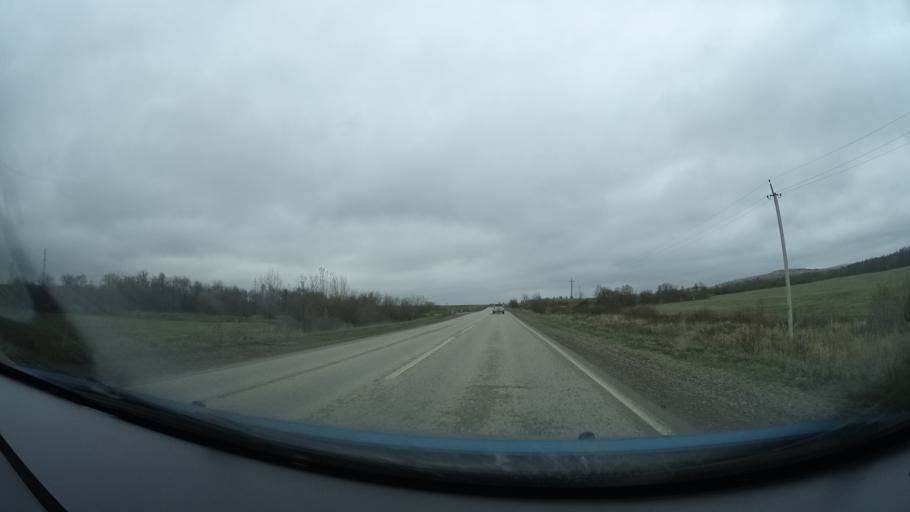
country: RU
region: Perm
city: Barda
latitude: 57.0577
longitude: 55.5428
